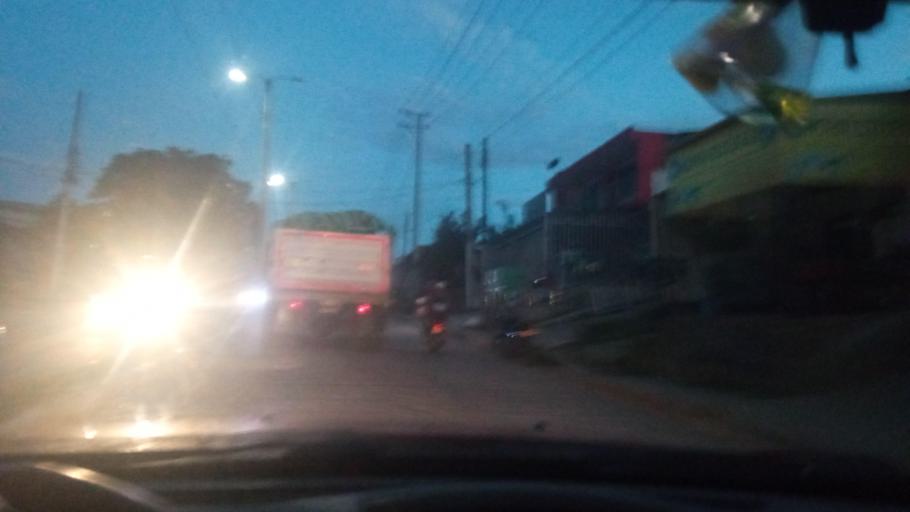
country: CO
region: Huila
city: Pitalito
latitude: 1.8585
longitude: -76.0478
